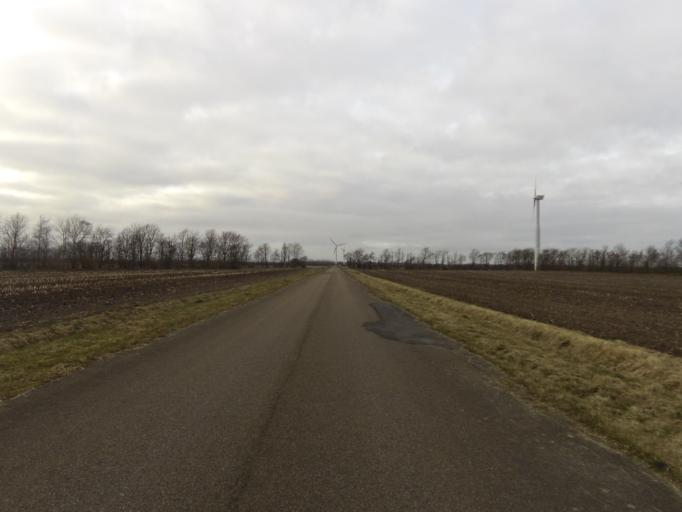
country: DK
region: South Denmark
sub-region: Tonder Kommune
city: Toftlund
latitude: 55.2373
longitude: 9.0739
